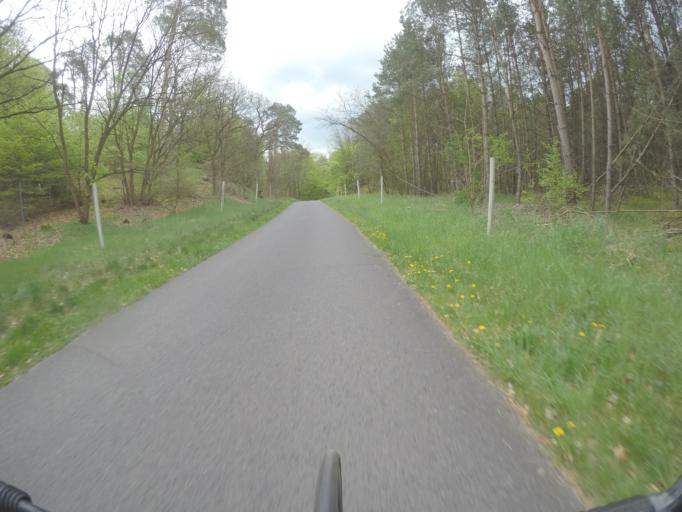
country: DE
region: Brandenburg
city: Biesenthal
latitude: 52.7924
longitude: 13.6306
